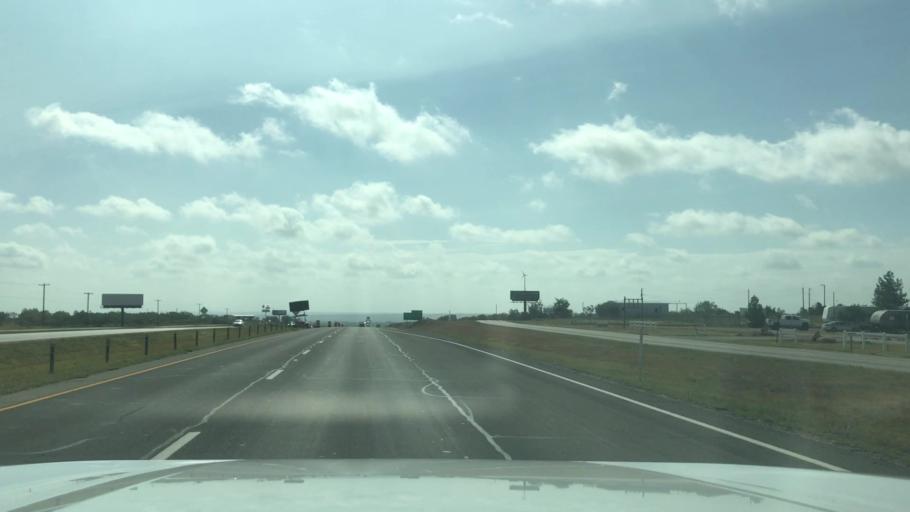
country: US
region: Texas
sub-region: Nolan County
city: Sweetwater
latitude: 32.4522
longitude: -100.4573
